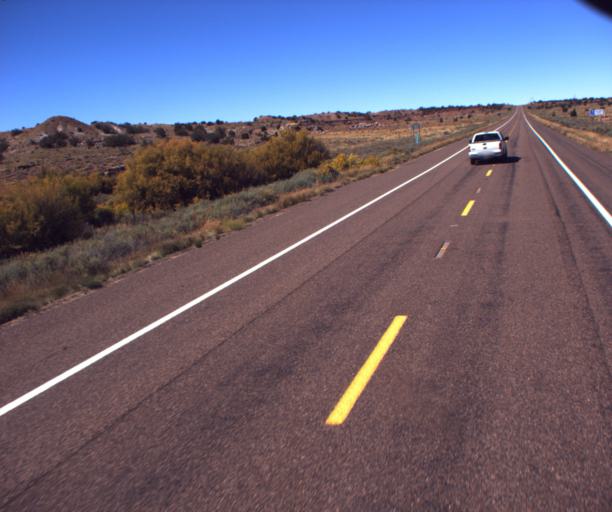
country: US
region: Arizona
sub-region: Apache County
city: Saint Johns
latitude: 34.6299
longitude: -109.6769
